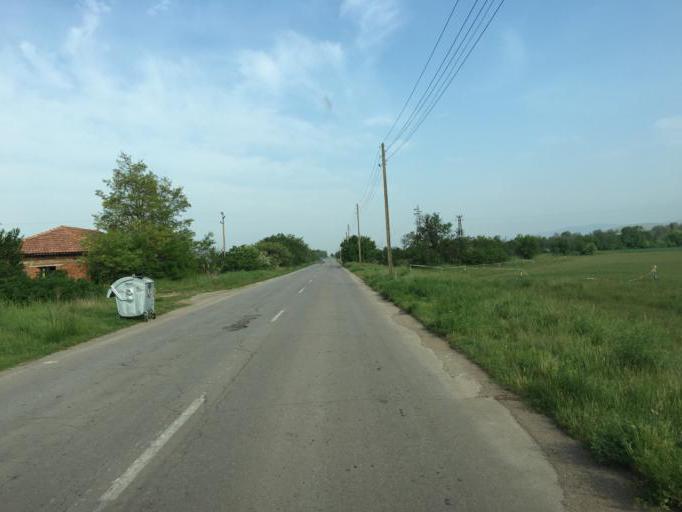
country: BG
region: Kyustendil
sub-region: Obshtina Bobovdol
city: Bobovdol
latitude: 42.4785
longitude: 23.0626
